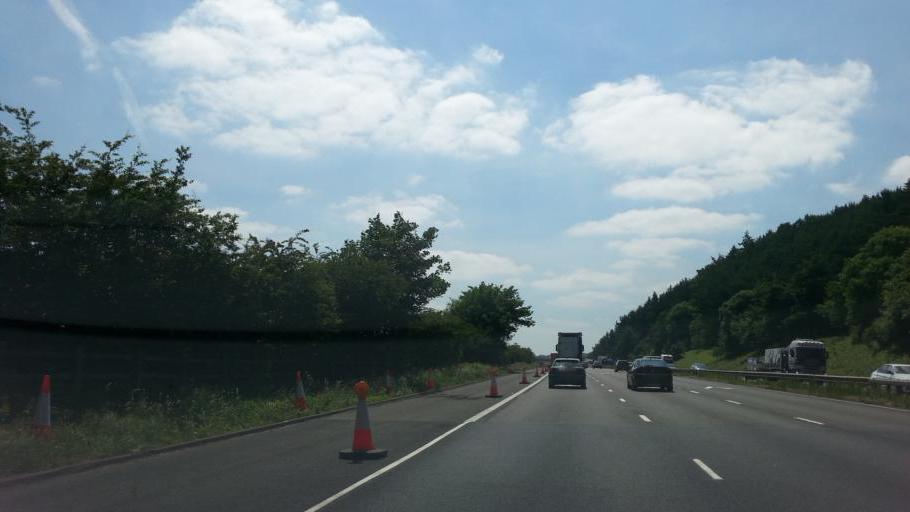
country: GB
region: England
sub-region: Staffordshire
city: Barlaston
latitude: 52.9408
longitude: -2.2158
